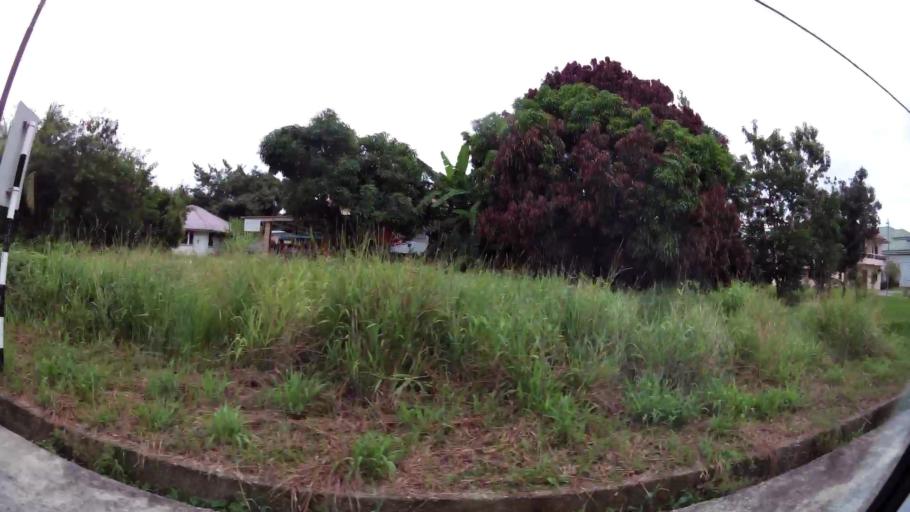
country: BN
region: Brunei and Muara
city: Bandar Seri Begawan
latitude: 4.8974
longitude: 114.9247
